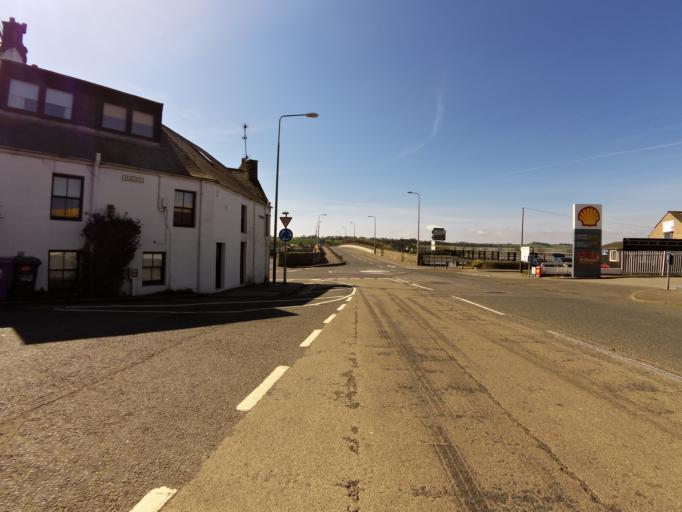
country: GB
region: Scotland
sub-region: Angus
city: Montrose
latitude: 56.7070
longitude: -2.4744
